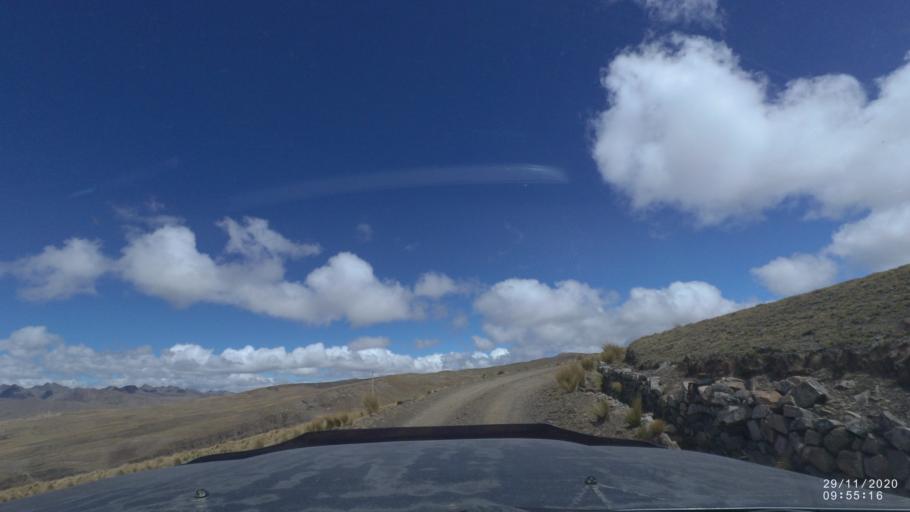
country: BO
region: Cochabamba
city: Cochabamba
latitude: -17.2755
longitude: -66.1787
